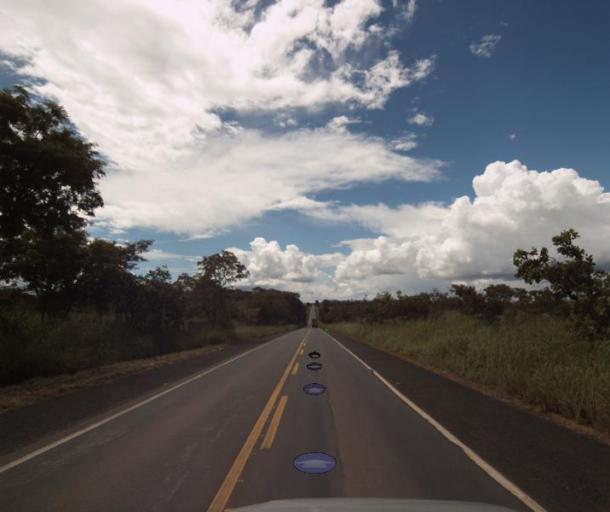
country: BR
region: Goias
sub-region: Uruacu
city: Uruacu
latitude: -14.1532
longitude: -49.1199
